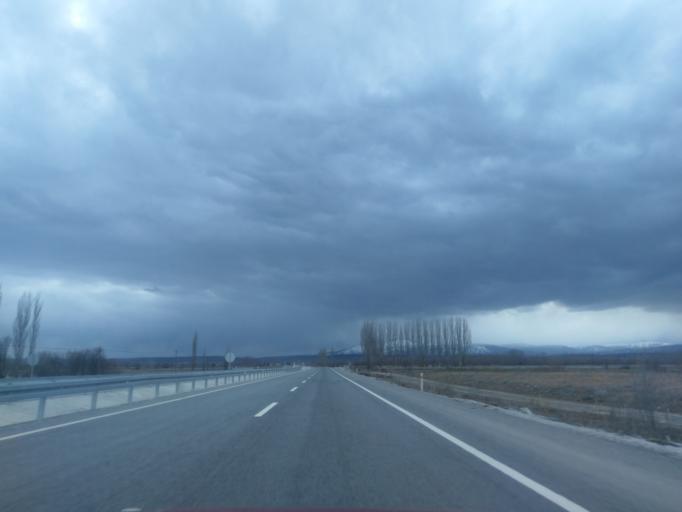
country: TR
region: Kuetahya
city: Cavdarhisar
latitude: 39.2116
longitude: 29.6509
